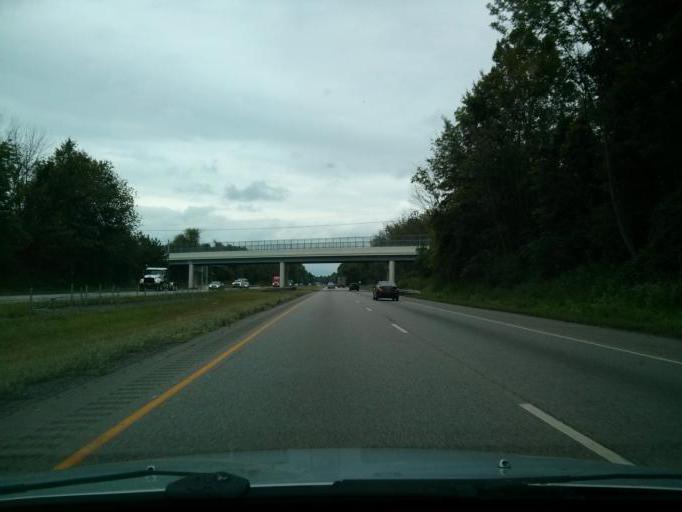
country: US
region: Ohio
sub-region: Portage County
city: Brimfield
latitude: 41.1088
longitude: -81.3145
